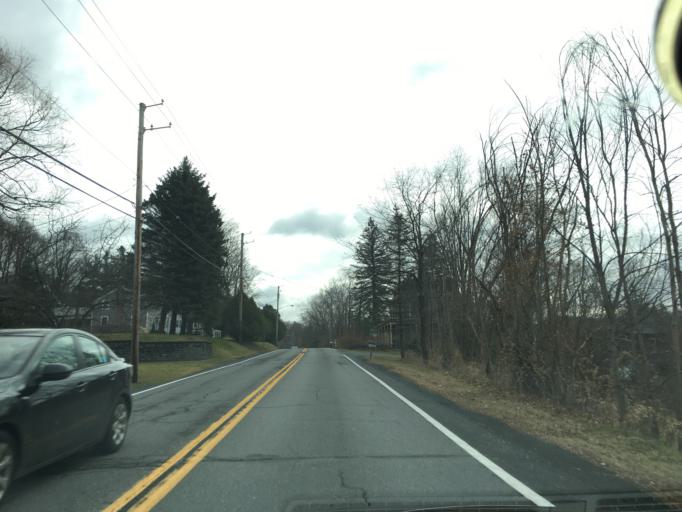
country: US
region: New York
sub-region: Rensselaer County
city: Averill Park
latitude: 42.6364
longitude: -73.5392
